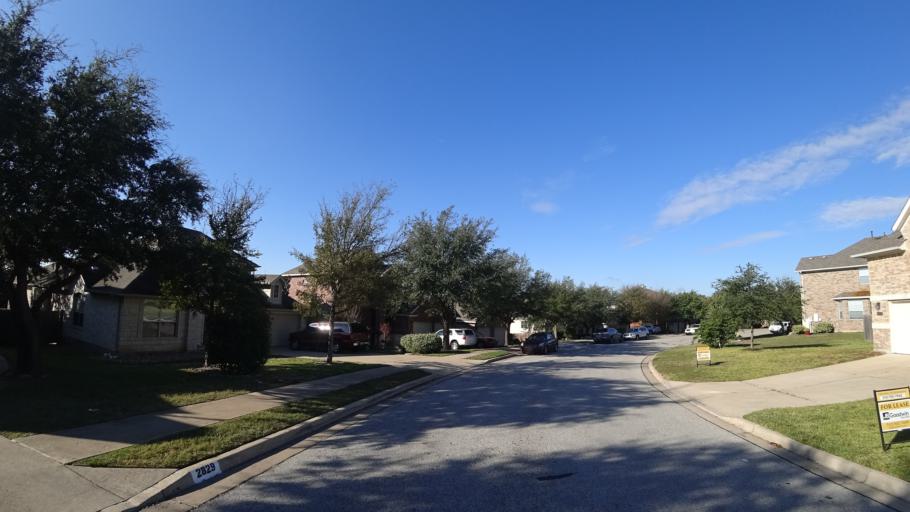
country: US
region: Texas
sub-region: Travis County
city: Hudson Bend
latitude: 30.3679
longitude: -97.8954
